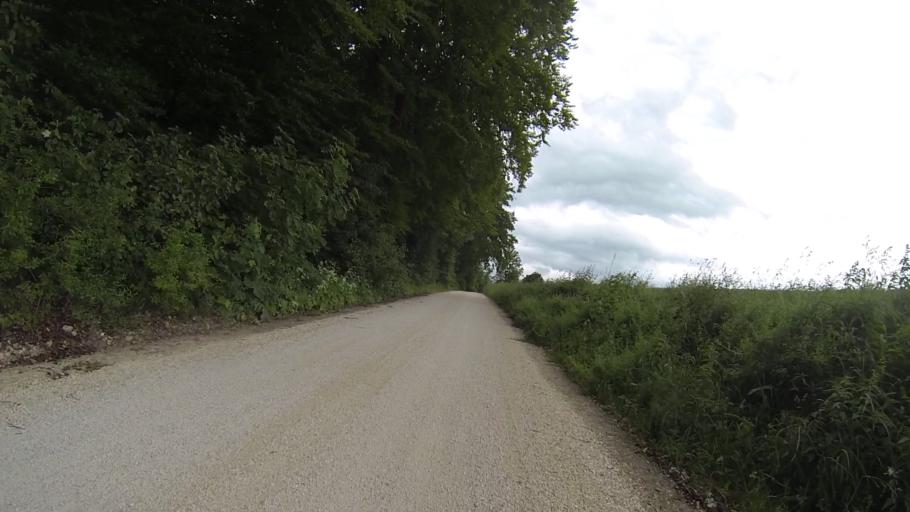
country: DE
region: Baden-Wuerttemberg
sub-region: Tuebingen Region
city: Dornstadt
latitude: 48.4234
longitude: 9.8793
